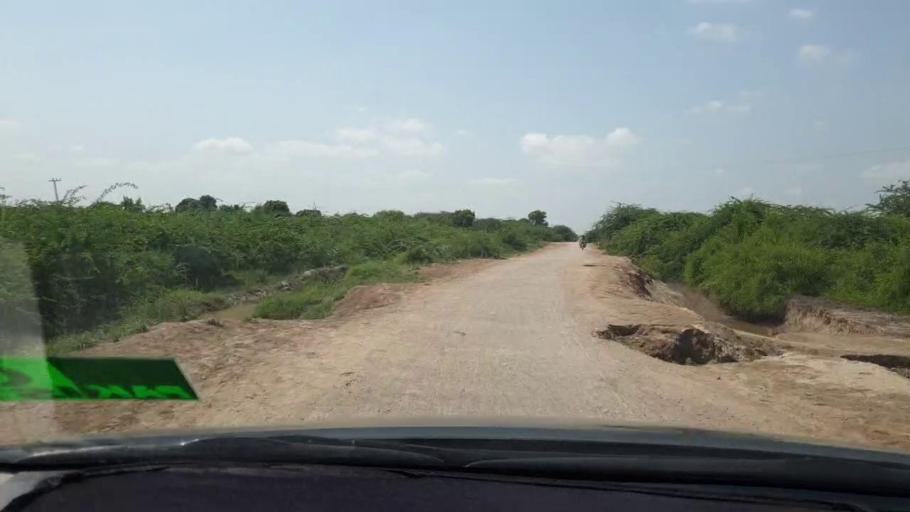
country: PK
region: Sindh
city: Naukot
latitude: 24.8849
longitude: 69.2206
